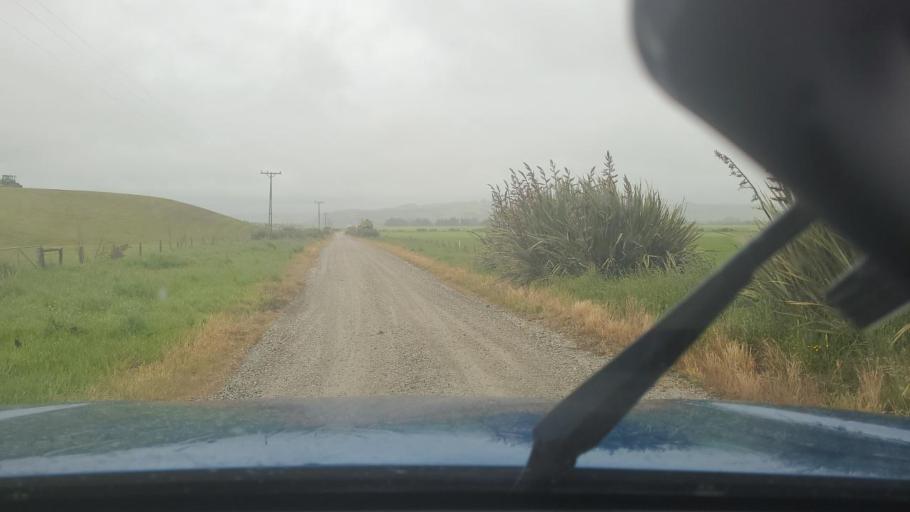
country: NZ
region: Southland
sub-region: Gore District
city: Gore
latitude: -46.4019
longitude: 168.7516
